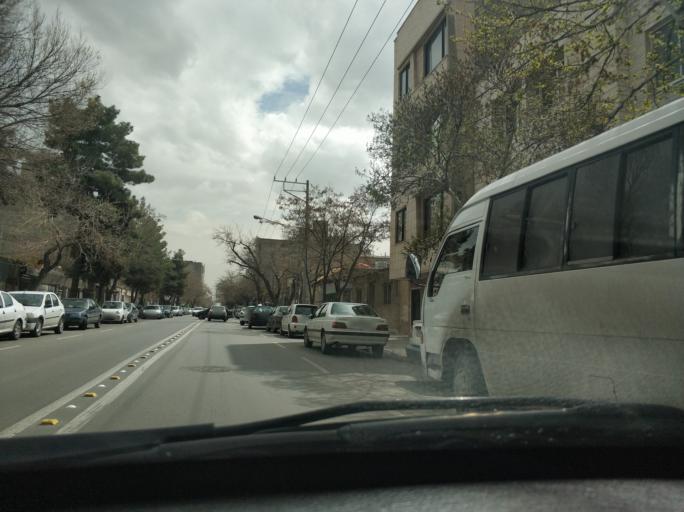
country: IR
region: Razavi Khorasan
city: Mashhad
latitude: 36.2820
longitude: 59.5727
